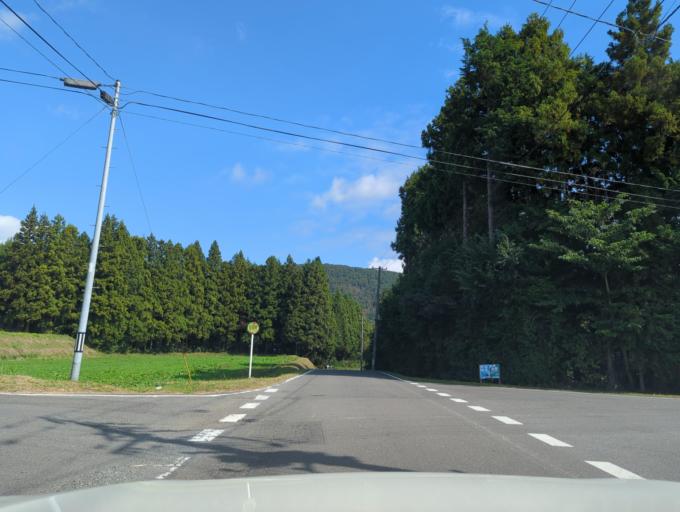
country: JP
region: Fukushima
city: Motomiya
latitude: 37.5569
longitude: 140.3481
